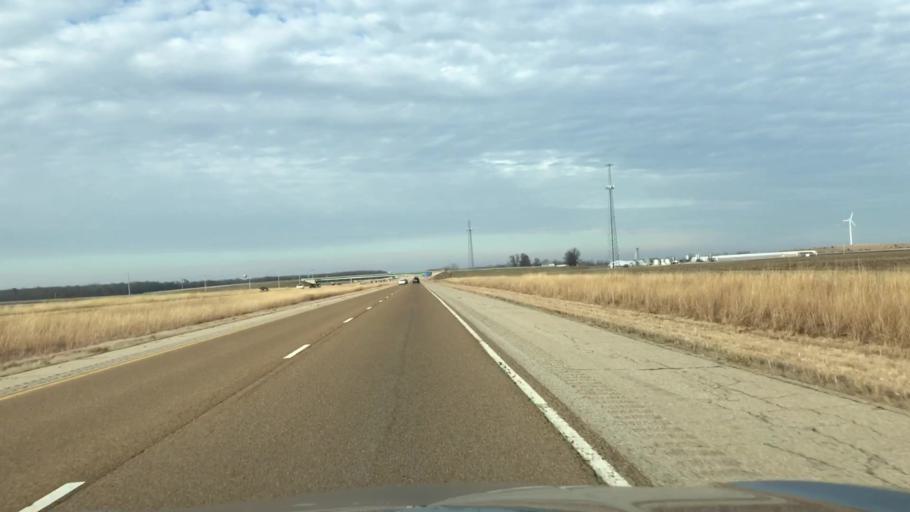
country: US
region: Illinois
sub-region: Montgomery County
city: Raymond
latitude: 39.4150
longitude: -89.6432
